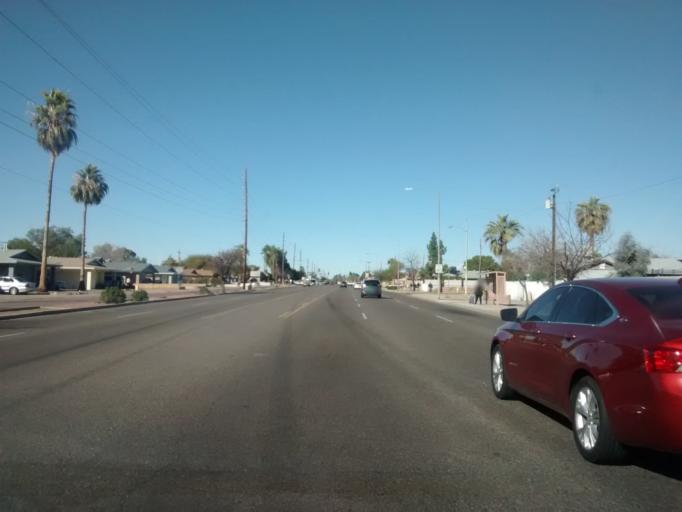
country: US
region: Arizona
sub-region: Maricopa County
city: Glendale
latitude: 33.5927
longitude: -112.1340
